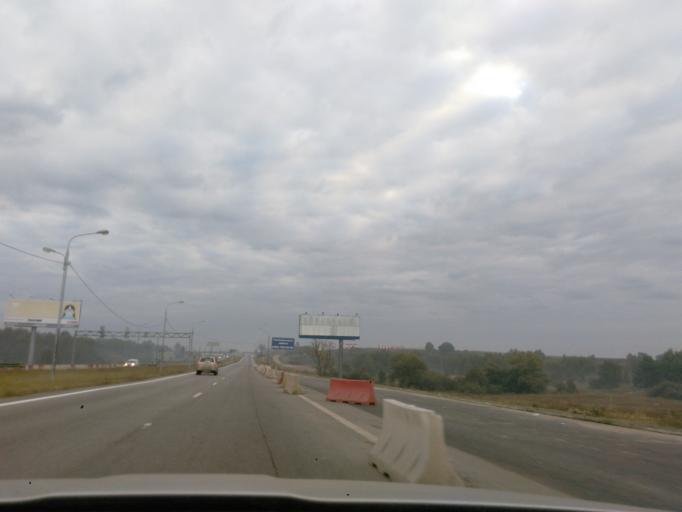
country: RU
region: Moskovskaya
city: Novopodrezkovo
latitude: 55.9650
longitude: 37.3644
